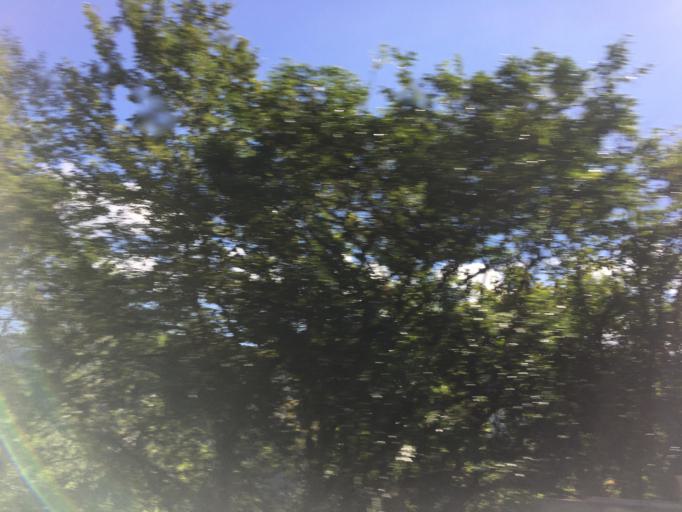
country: TW
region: Taiwan
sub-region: Yilan
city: Yilan
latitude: 24.5049
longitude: 121.5694
